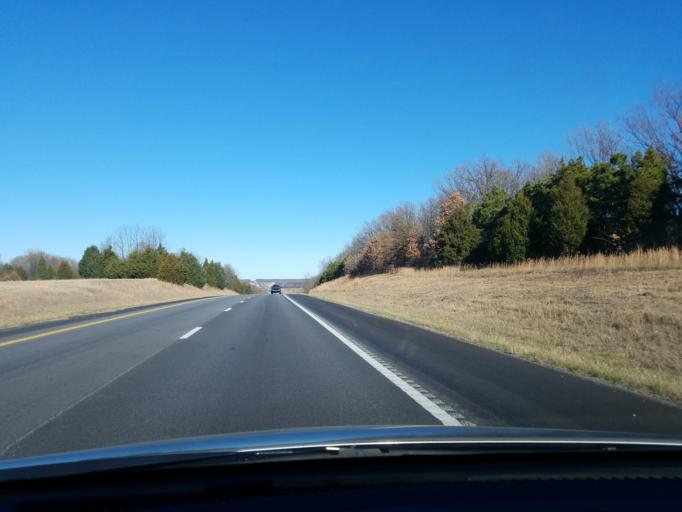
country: US
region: Missouri
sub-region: Webster County
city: Marshfield
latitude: 37.4016
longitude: -92.8954
